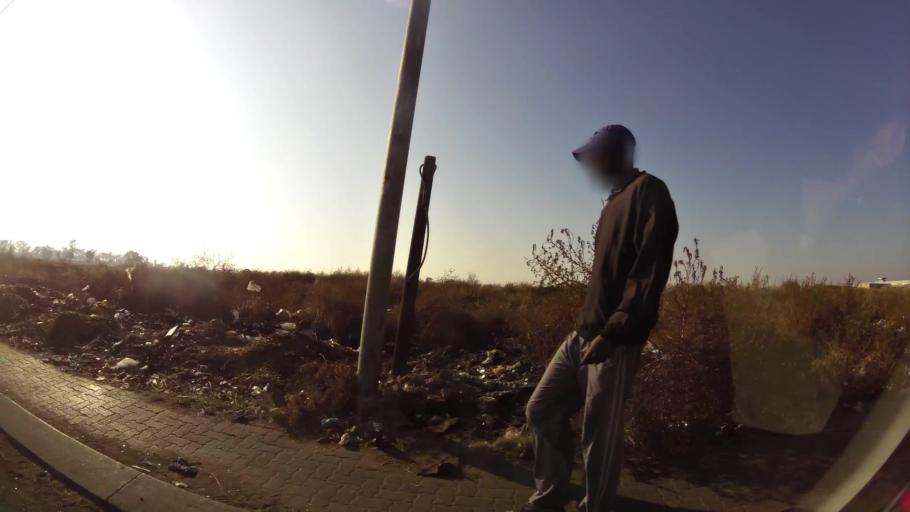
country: ZA
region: Orange Free State
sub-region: Mangaung Metropolitan Municipality
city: Bloemfontein
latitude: -29.1370
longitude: 26.2520
